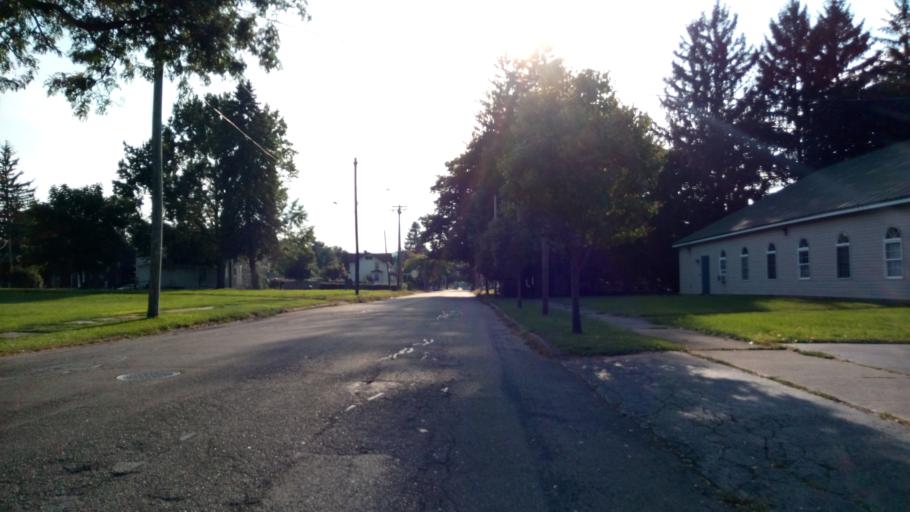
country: US
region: New York
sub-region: Chemung County
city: Elmira Heights
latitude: 42.1126
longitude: -76.8097
